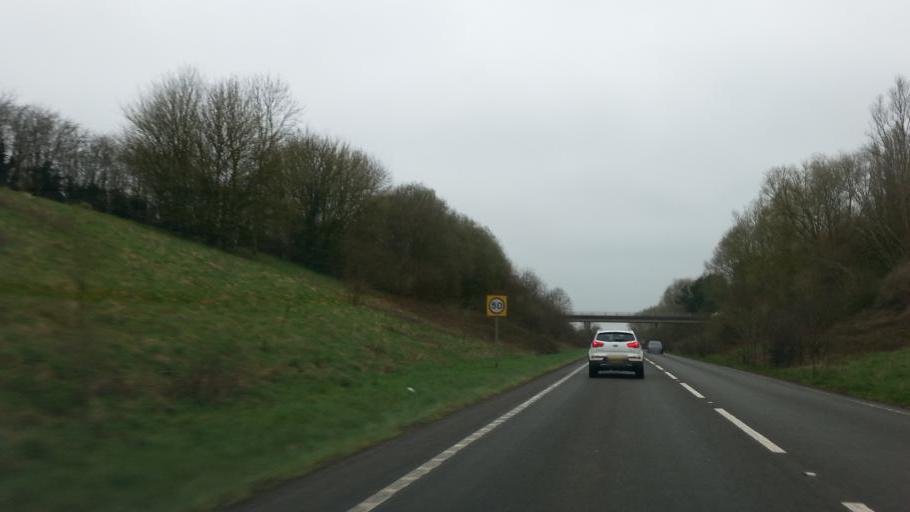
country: GB
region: England
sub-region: Oxfordshire
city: Adderbury
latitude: 52.0687
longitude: -1.2709
